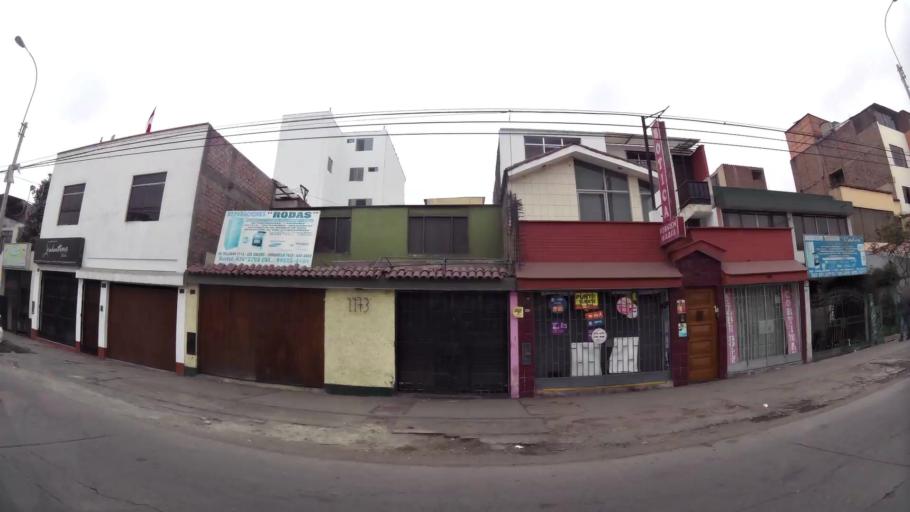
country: PE
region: Lima
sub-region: Lima
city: Surco
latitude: -12.1200
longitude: -76.9993
